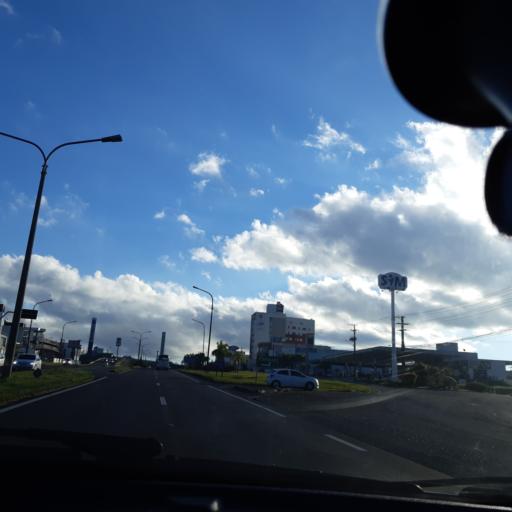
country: BR
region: Rio Grande do Sul
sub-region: Caxias Do Sul
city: Caxias do Sul
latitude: -29.1753
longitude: -51.2124
